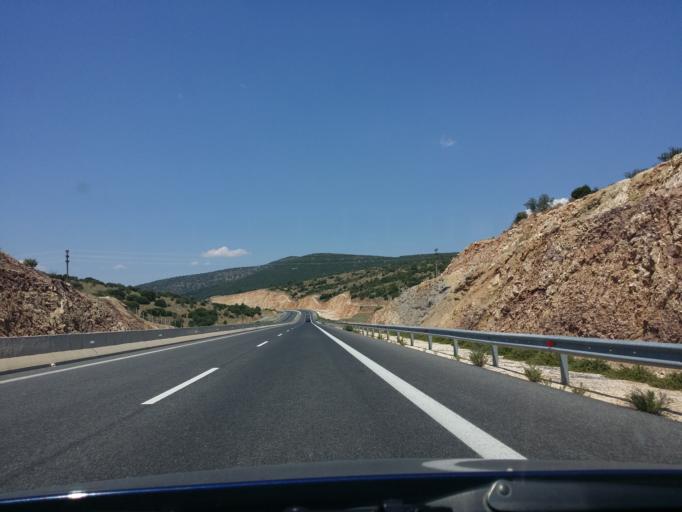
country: GR
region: Peloponnese
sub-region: Nomos Arkadias
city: Tripoli
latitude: 37.3966
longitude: 22.2957
